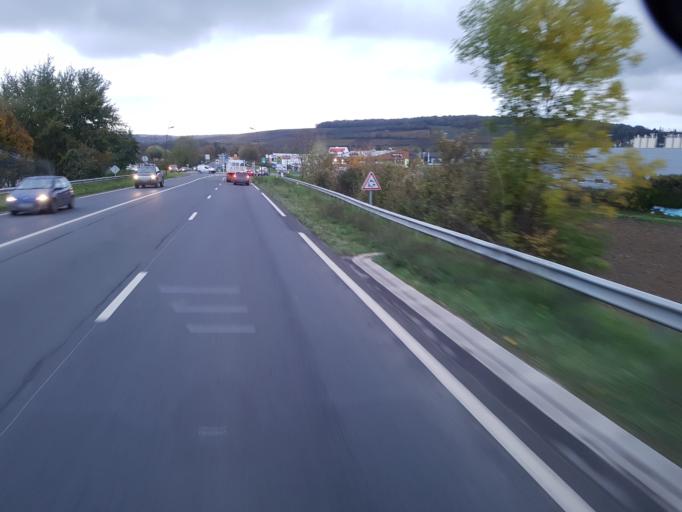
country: FR
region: Picardie
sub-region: Departement de l'Aisne
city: Chateau-Thierry
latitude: 49.0334
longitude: 3.3941
